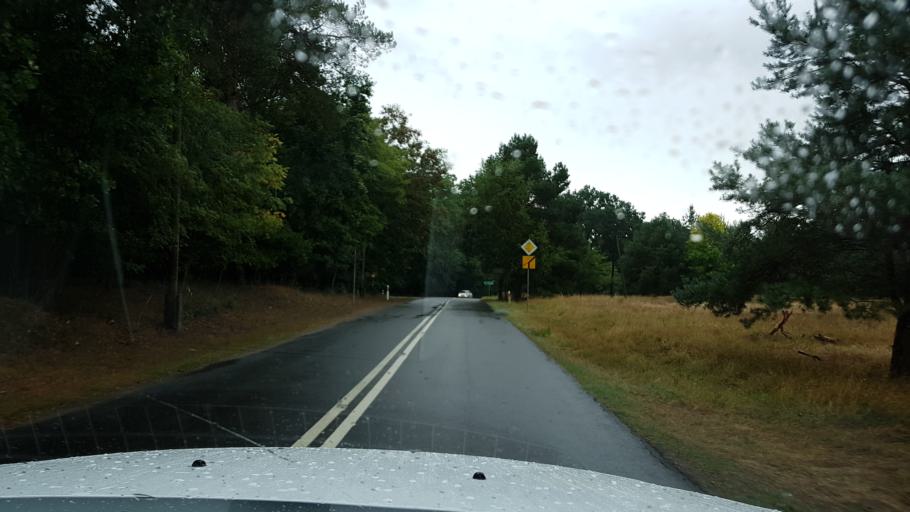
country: PL
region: West Pomeranian Voivodeship
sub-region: Powiat gryfinski
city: Cedynia
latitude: 52.9205
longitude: 14.2043
